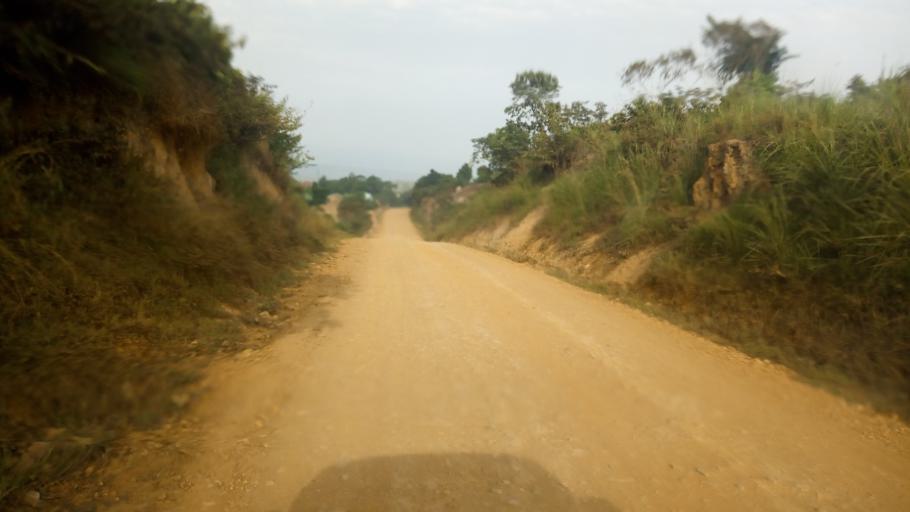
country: UG
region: Western Region
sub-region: Kanungu District
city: Ntungamo
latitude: -0.8335
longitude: 29.6902
